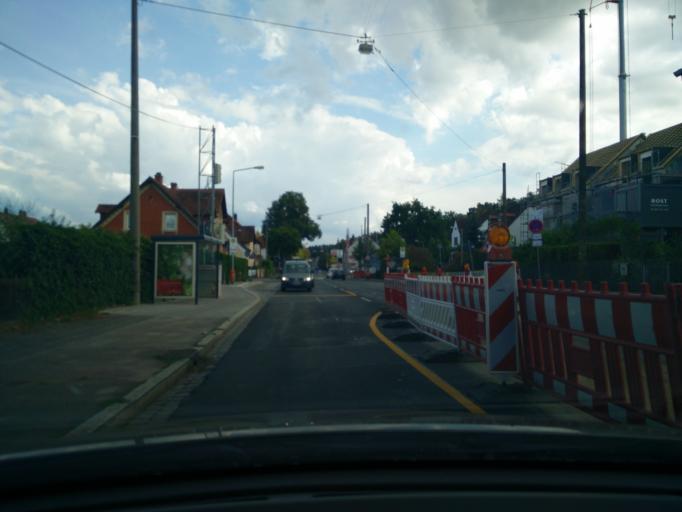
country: DE
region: Bavaria
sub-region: Regierungsbezirk Mittelfranken
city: Stein
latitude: 49.3746
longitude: 11.0259
